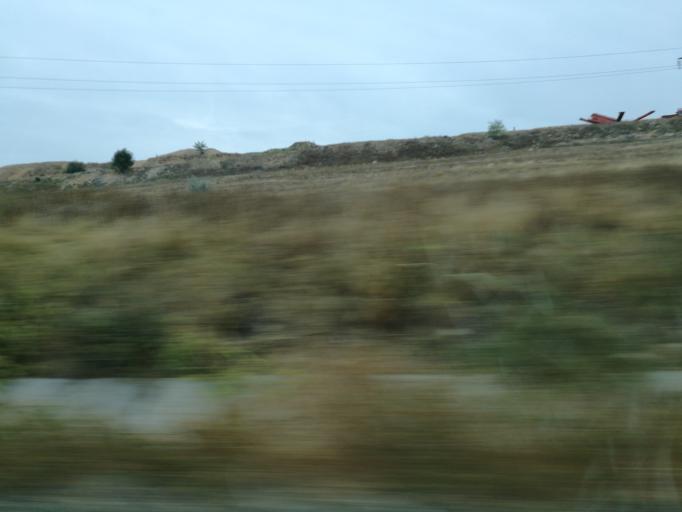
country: RO
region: Constanta
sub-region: Comuna Mihail Kogalniceanu
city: Piatra
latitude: 44.4165
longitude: 28.5327
